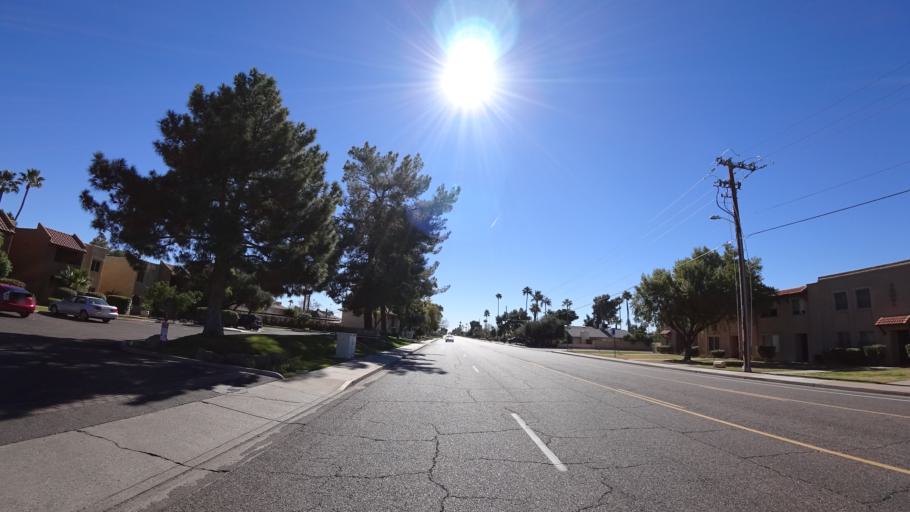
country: US
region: Arizona
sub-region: Maricopa County
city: Scottsdale
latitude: 33.5215
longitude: -111.9001
